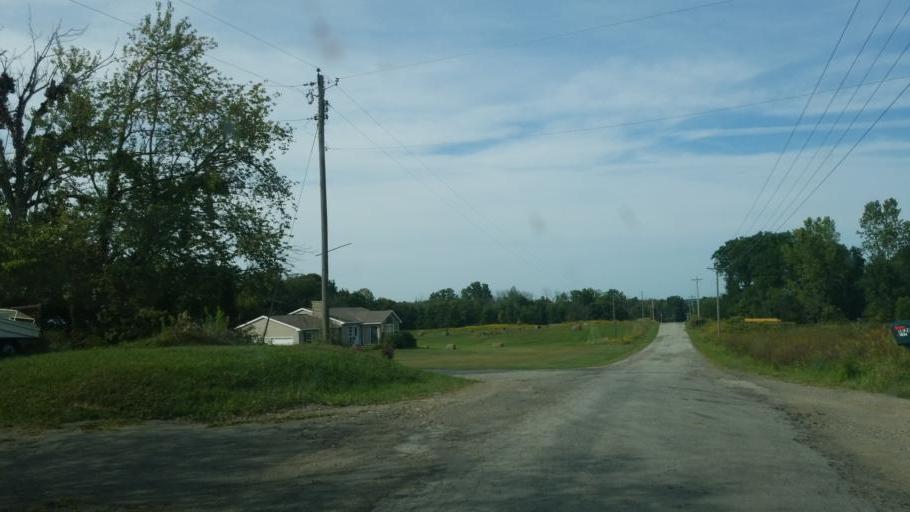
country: US
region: Ohio
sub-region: Knox County
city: Centerburg
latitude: 40.4118
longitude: -82.6513
